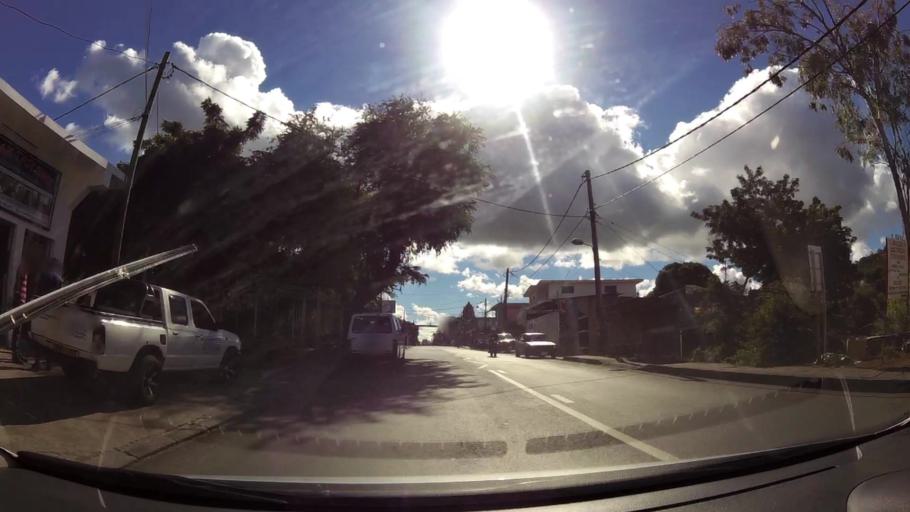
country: MU
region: Pamplemousses
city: Le Hochet
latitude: -20.1352
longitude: 57.5275
